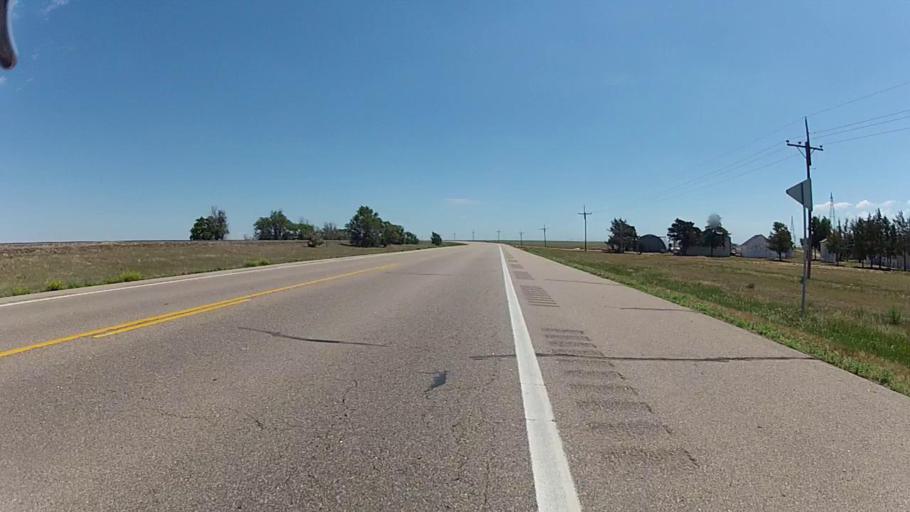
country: US
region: Kansas
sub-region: Gray County
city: Cimarron
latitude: 37.6648
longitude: -100.2039
